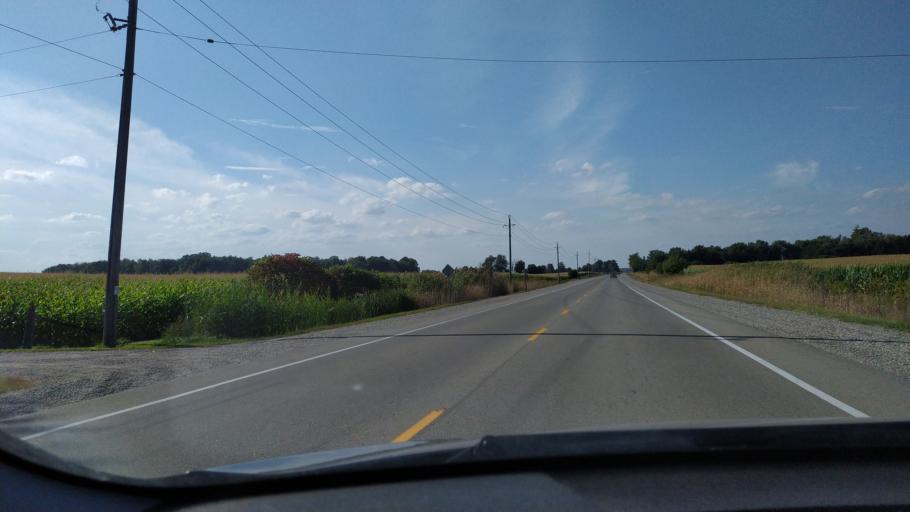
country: CA
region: Ontario
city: Ingersoll
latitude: 43.0555
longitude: -80.8281
